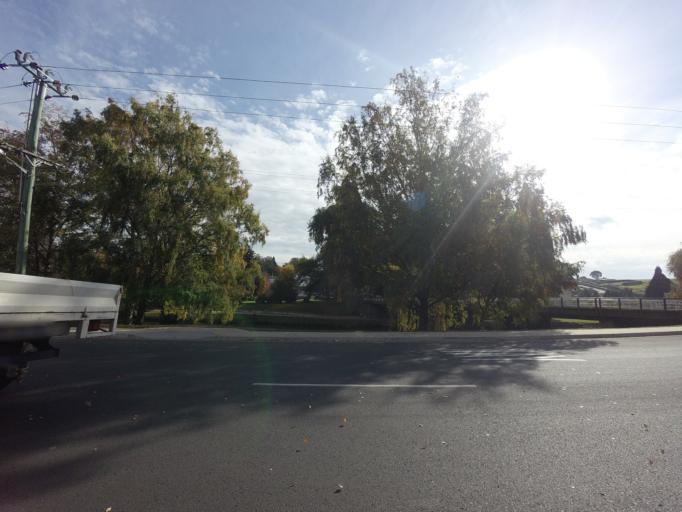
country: AU
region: Tasmania
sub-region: Meander Valley
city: Deloraine
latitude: -41.5251
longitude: 146.6587
